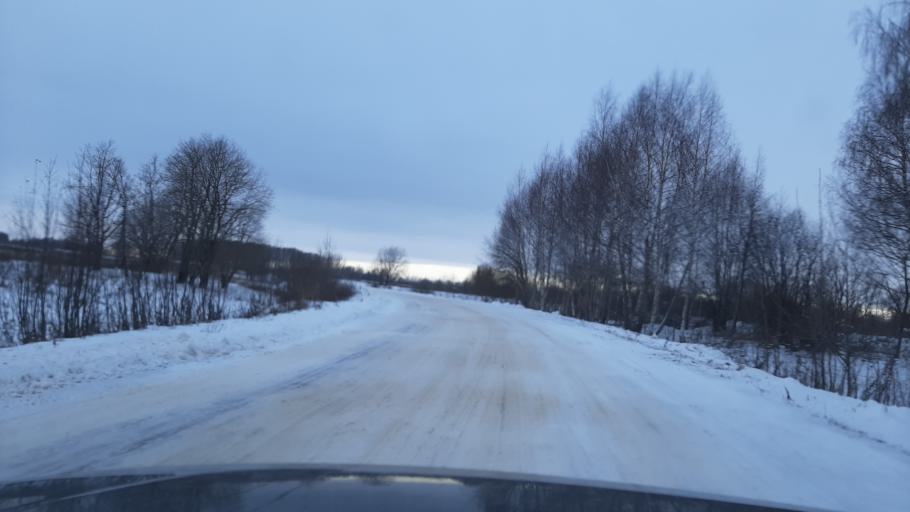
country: RU
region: Kostroma
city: Volgorechensk
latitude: 57.4491
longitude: 41.0289
